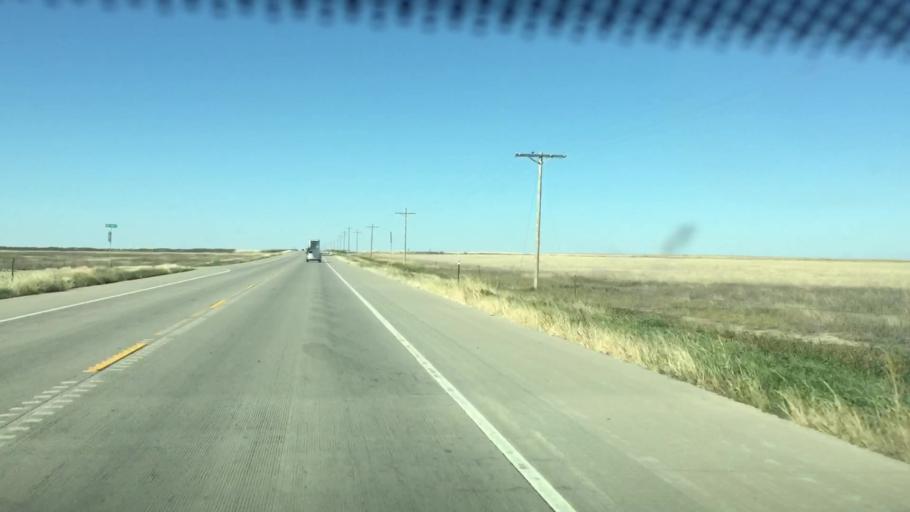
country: US
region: Colorado
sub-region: Prowers County
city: Lamar
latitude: 38.2341
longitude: -102.7240
